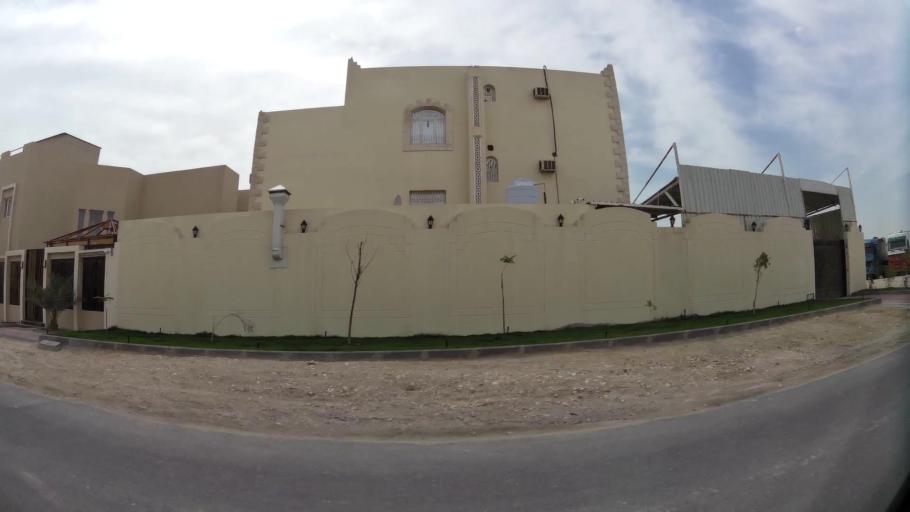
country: QA
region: Baladiyat ad Dawhah
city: Doha
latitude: 25.2153
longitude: 51.4738
